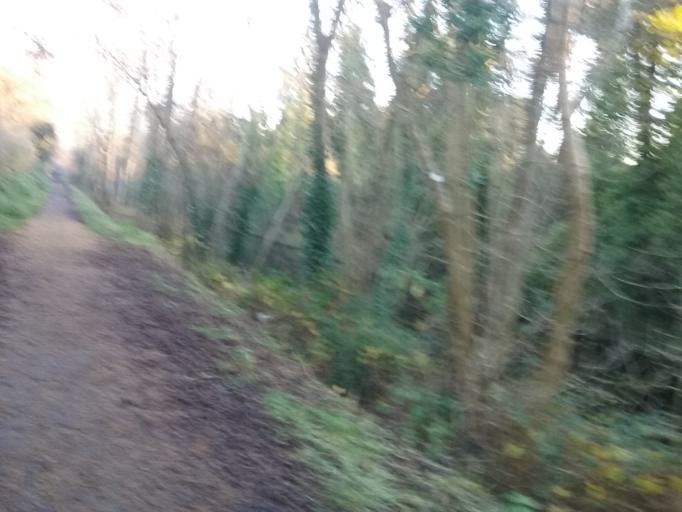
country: IE
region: Leinster
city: Hartstown
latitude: 53.3828
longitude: -6.4215
